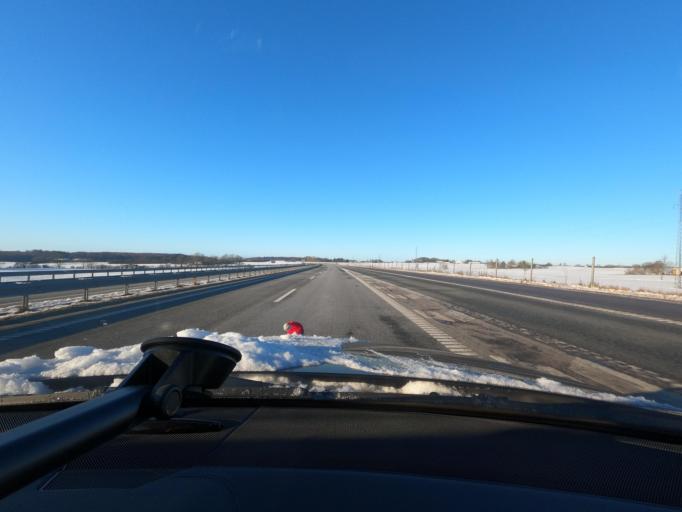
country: DK
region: South Denmark
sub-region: Sonderborg Kommune
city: Grasten
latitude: 54.9550
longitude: 9.6286
